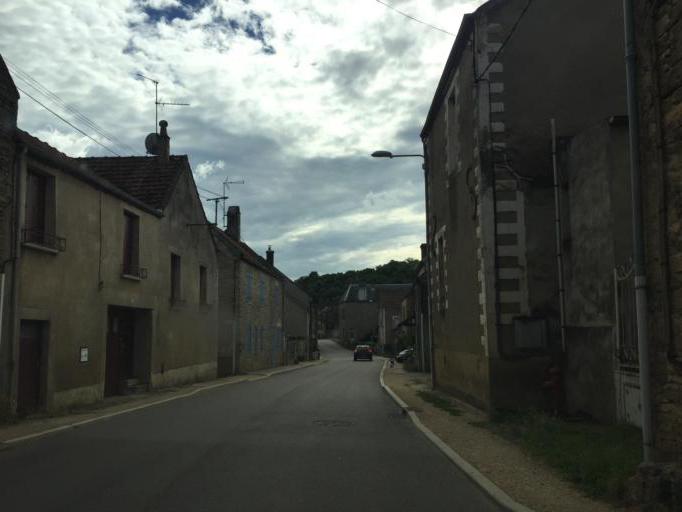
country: FR
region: Bourgogne
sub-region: Departement de l'Yonne
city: Avallon
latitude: 47.4617
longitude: 3.7668
